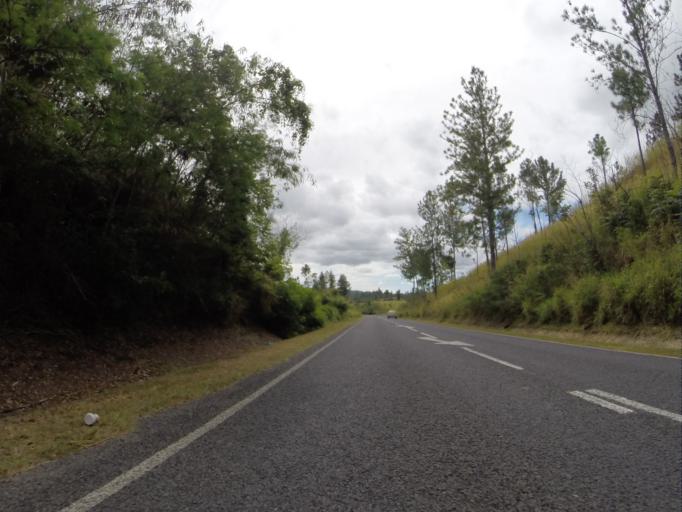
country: FJ
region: Western
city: Nadi
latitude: -17.9929
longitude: 177.3214
